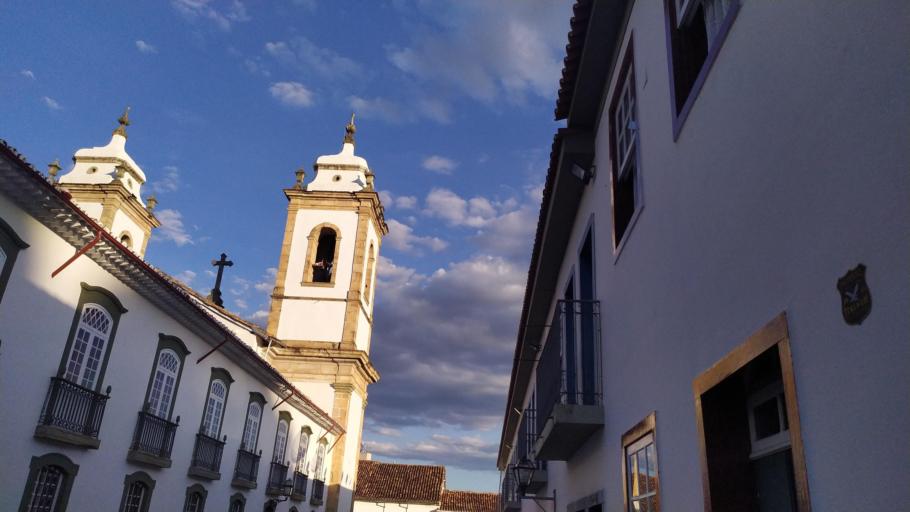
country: BR
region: Minas Gerais
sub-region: Sao Joao Del Rei
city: Sao Joao del Rei
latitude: -21.1352
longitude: -44.2624
